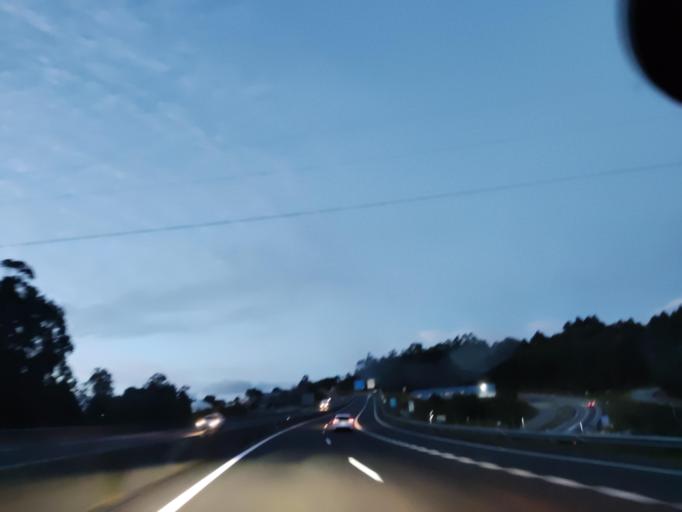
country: ES
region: Galicia
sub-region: Provincia da Coruna
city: Boiro
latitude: 42.6608
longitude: -8.8729
